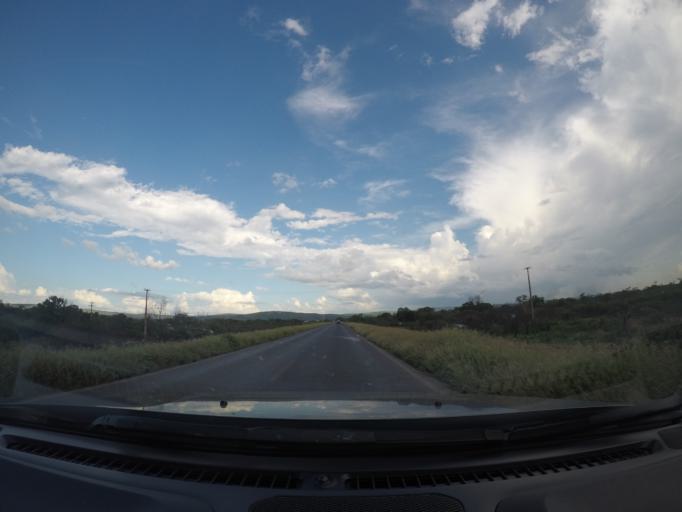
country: BR
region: Bahia
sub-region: Ibotirama
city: Ibotirama
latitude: -12.1807
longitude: -43.2384
